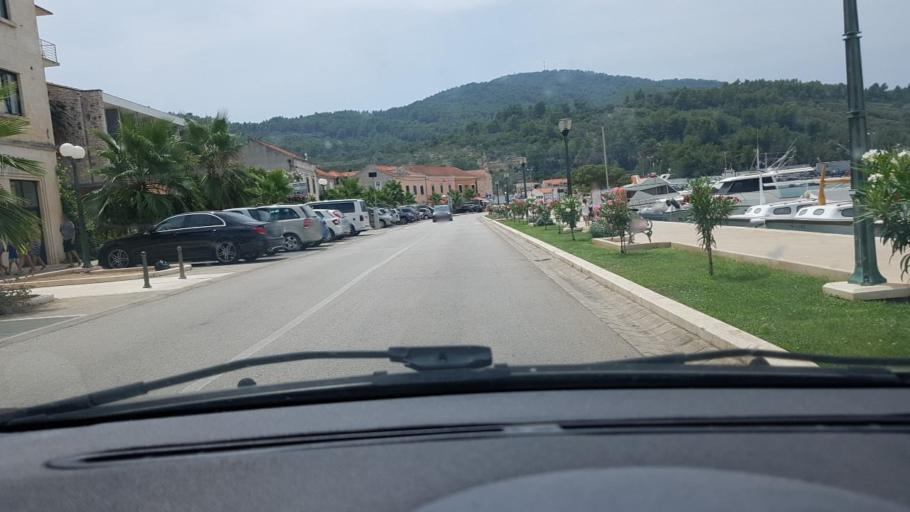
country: HR
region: Dubrovacko-Neretvanska
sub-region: Grad Dubrovnik
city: Vela Luka
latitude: 42.9597
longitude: 16.7129
